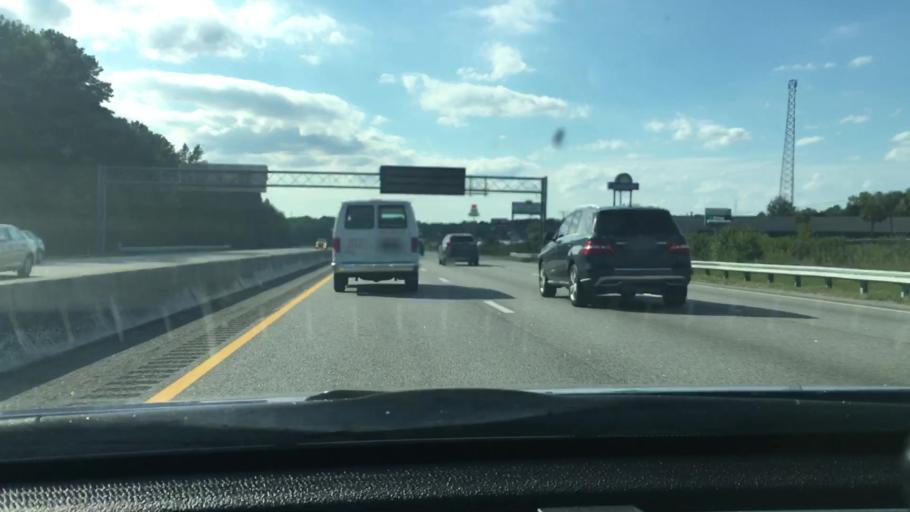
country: US
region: South Carolina
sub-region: Richland County
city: Dentsville
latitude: 34.0735
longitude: -80.9914
